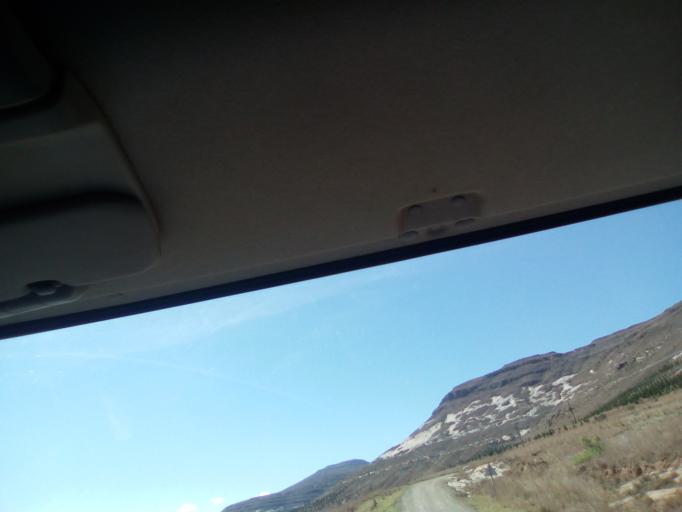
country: LS
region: Qacha's Nek
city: Qacha's Nek
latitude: -30.0351
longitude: 28.6707
